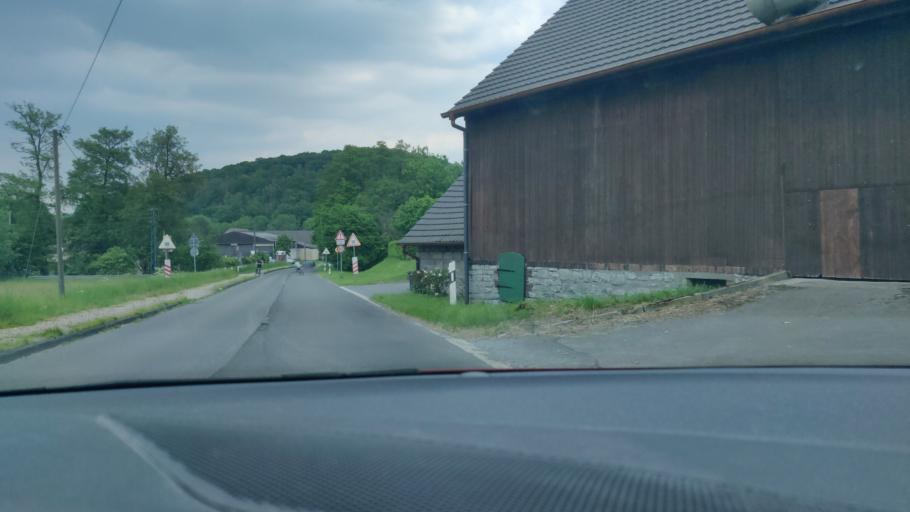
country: DE
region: North Rhine-Westphalia
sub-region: Regierungsbezirk Dusseldorf
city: Velbert
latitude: 51.3382
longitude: 7.0919
